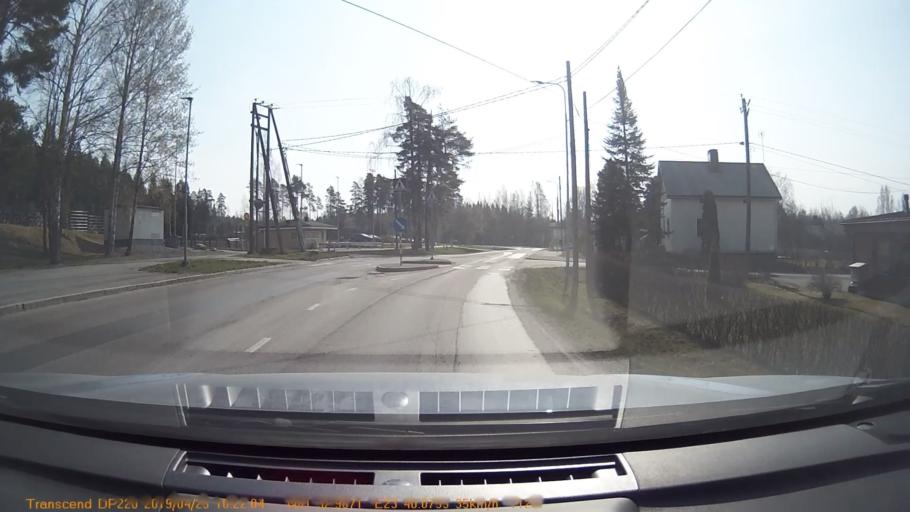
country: FI
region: Pirkanmaa
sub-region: Tampere
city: Yloejaervi
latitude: 61.5494
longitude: 23.6675
